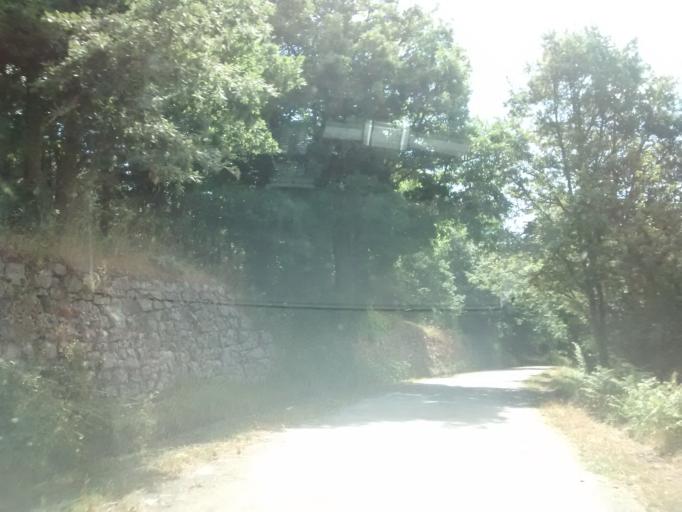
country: ES
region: Castille and Leon
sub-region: Provincia de Palencia
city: Berzosilla
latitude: 42.8805
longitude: -4.0512
